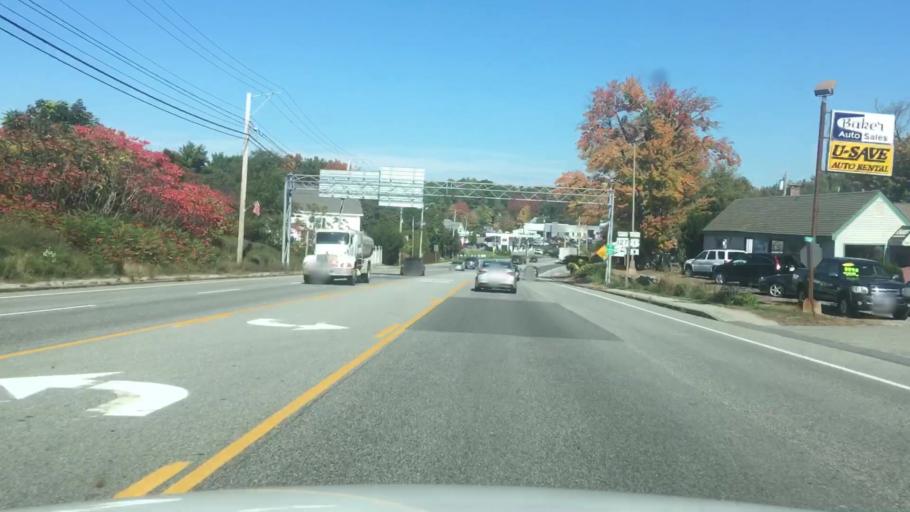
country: US
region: Maine
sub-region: Sagadahoc County
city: Woolwich
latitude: 43.9151
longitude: -69.8015
